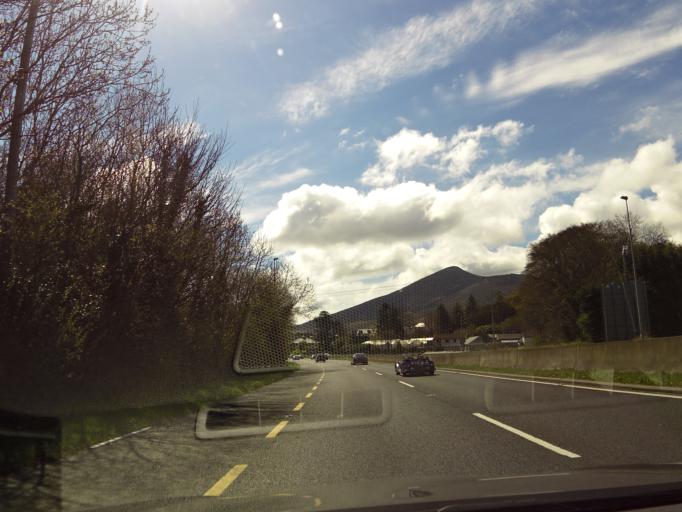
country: IE
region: Leinster
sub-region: Wicklow
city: Kilmacanoge
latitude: 53.1754
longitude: -6.1385
